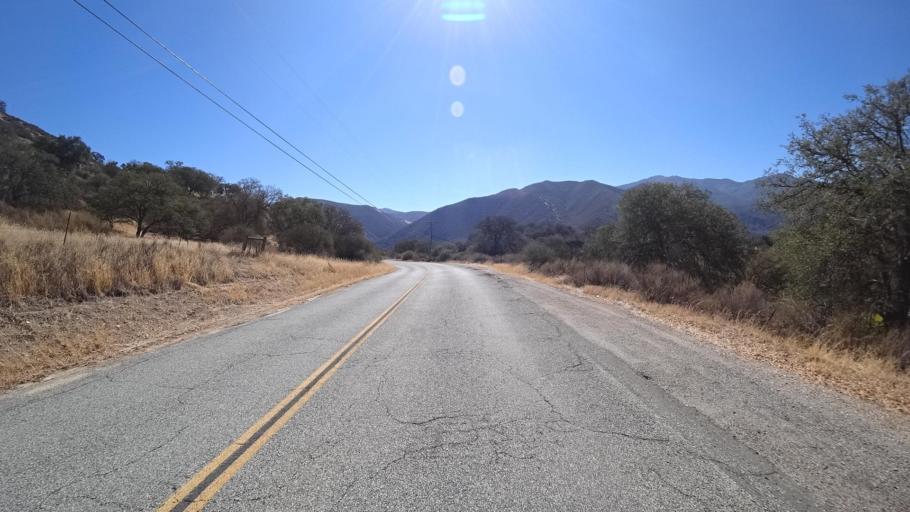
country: US
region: California
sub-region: Monterey County
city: Soledad
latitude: 36.2624
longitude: -121.4279
